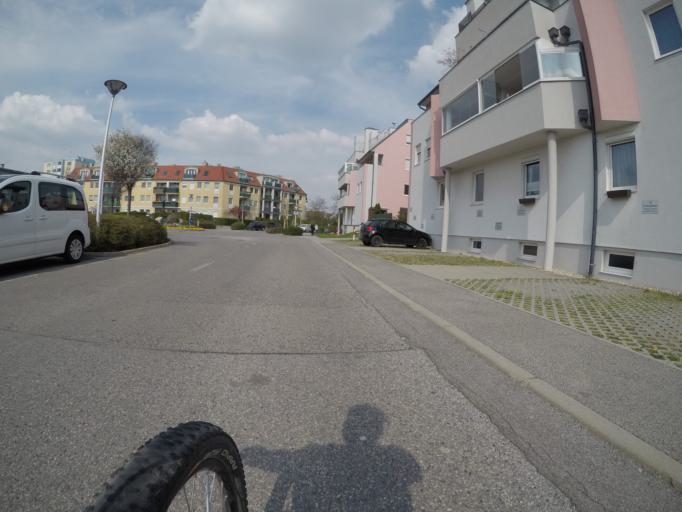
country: AT
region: Lower Austria
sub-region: Politischer Bezirk Modling
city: Wiener Neudorf
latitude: 48.0806
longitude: 16.3121
